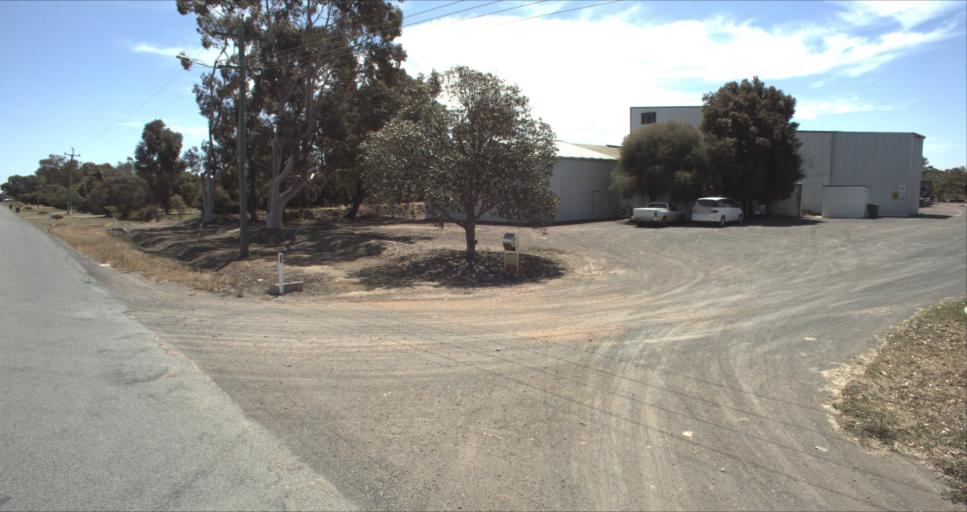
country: AU
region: New South Wales
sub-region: Leeton
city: Leeton
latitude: -34.5721
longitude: 146.4172
